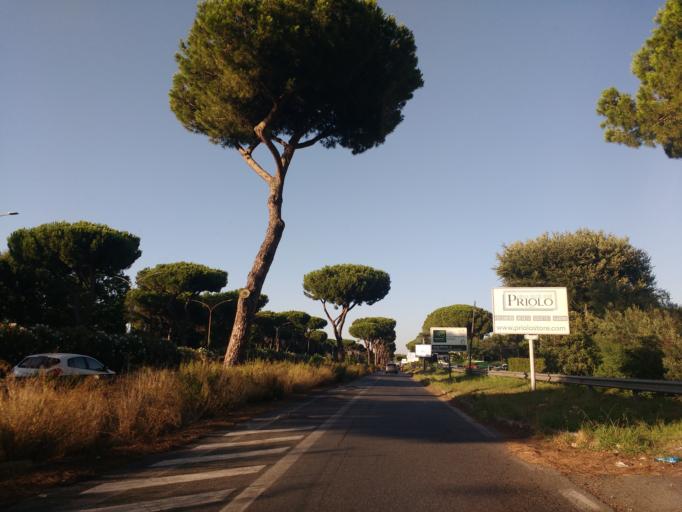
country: IT
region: Latium
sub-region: Citta metropolitana di Roma Capitale
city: Acilia-Castel Fusano-Ostia Antica
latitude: 41.7467
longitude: 12.3593
